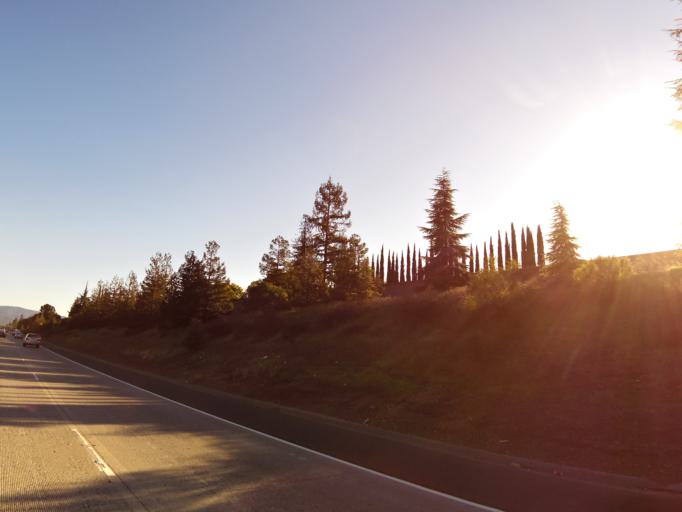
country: US
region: California
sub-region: Santa Clara County
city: Saratoga
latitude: 37.2934
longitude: -122.0256
